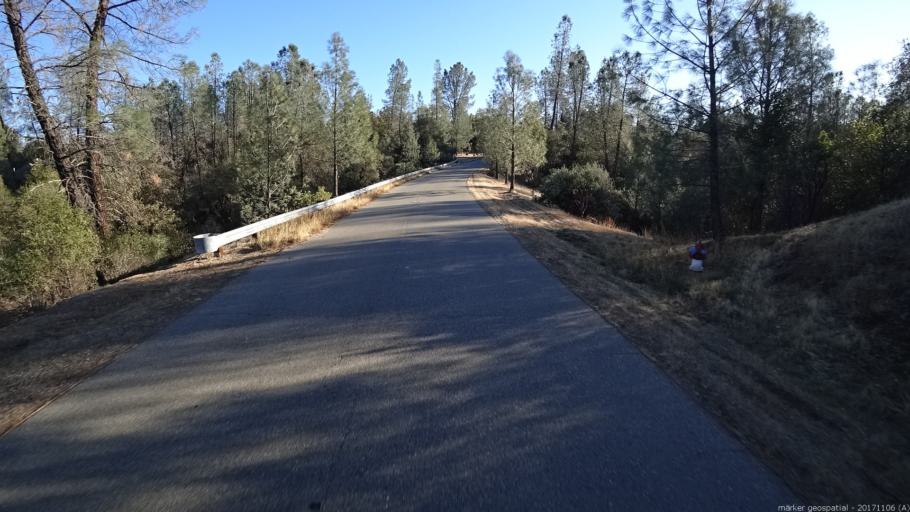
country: US
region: California
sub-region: Shasta County
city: Shasta
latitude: 40.5817
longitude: -122.4618
